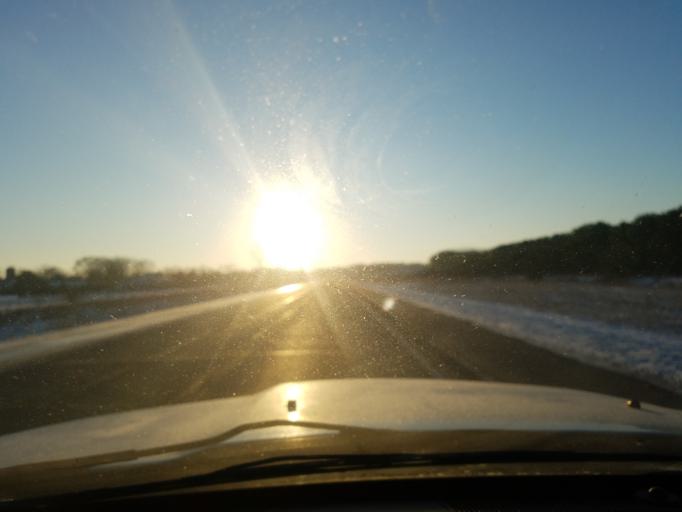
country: US
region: Indiana
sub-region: Marshall County
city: Bremen
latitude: 41.4587
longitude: -86.1394
